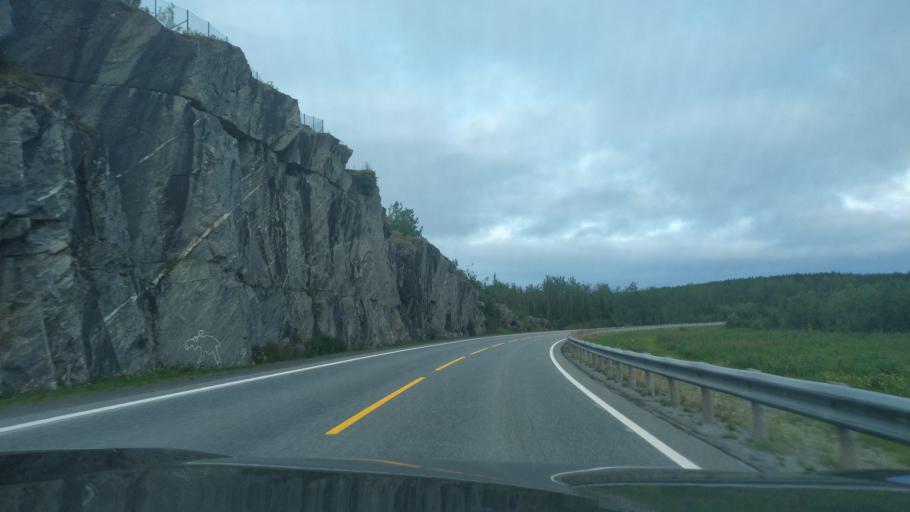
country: NO
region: Nordland
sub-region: Narvik
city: Narvik
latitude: 68.5317
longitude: 17.4141
